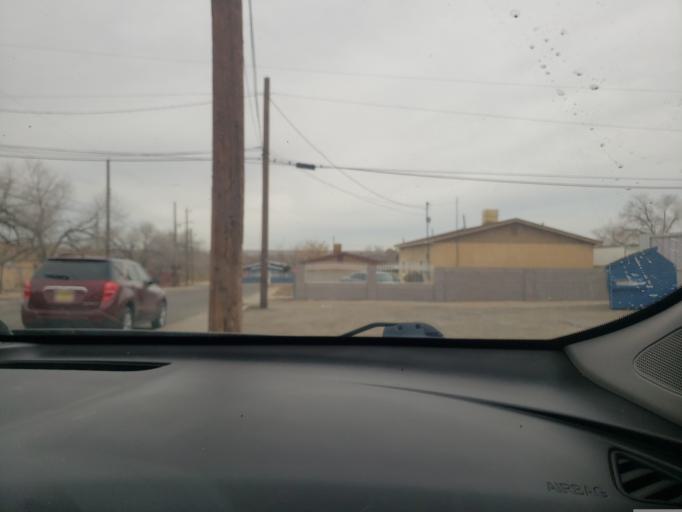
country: US
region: New Mexico
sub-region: Bernalillo County
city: Albuquerque
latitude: 35.0610
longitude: -106.6457
